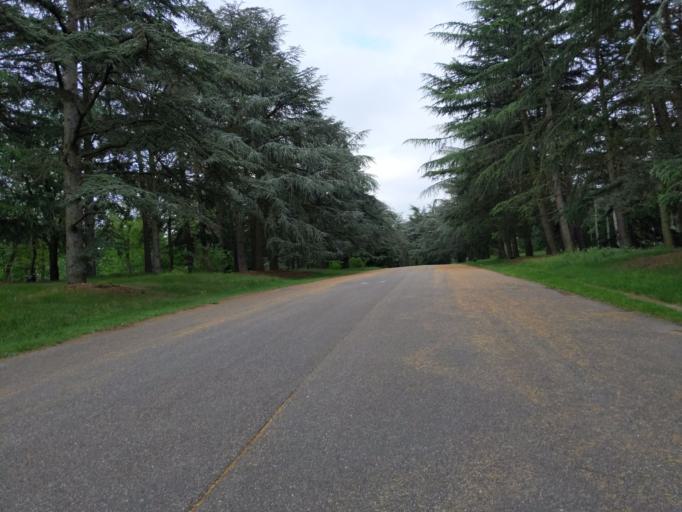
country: FR
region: Rhone-Alpes
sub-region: Departement du Rhone
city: Bron
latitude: 45.7230
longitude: 4.9010
